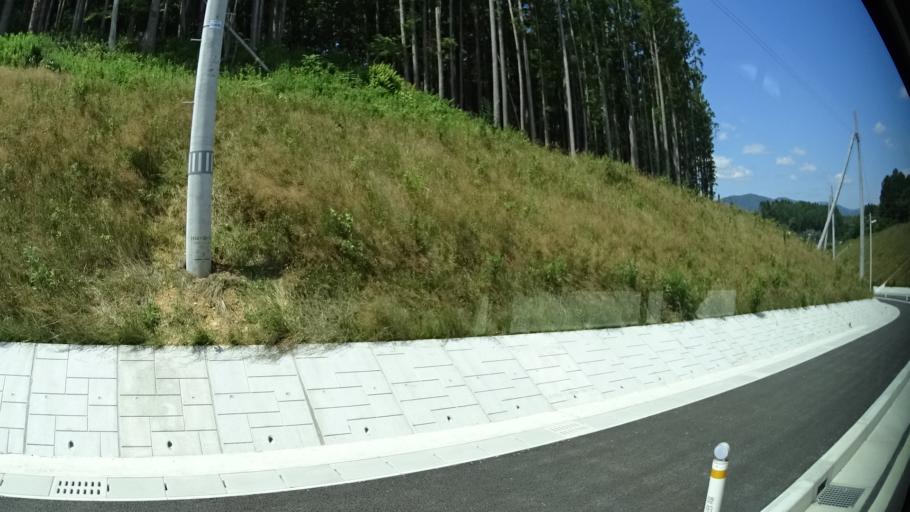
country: JP
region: Iwate
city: Ofunato
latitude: 39.0203
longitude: 141.6386
